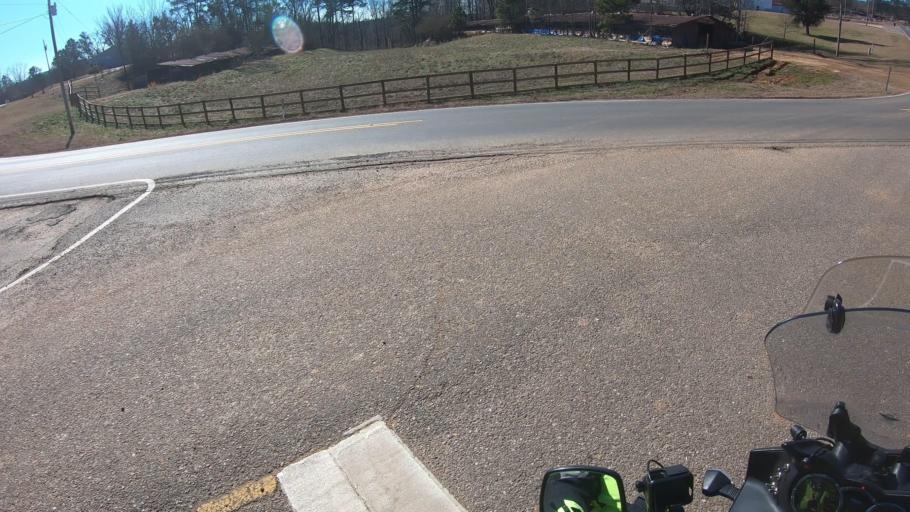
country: US
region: Alabama
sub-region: Clay County
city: Lineville
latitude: 33.4458
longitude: -85.7710
